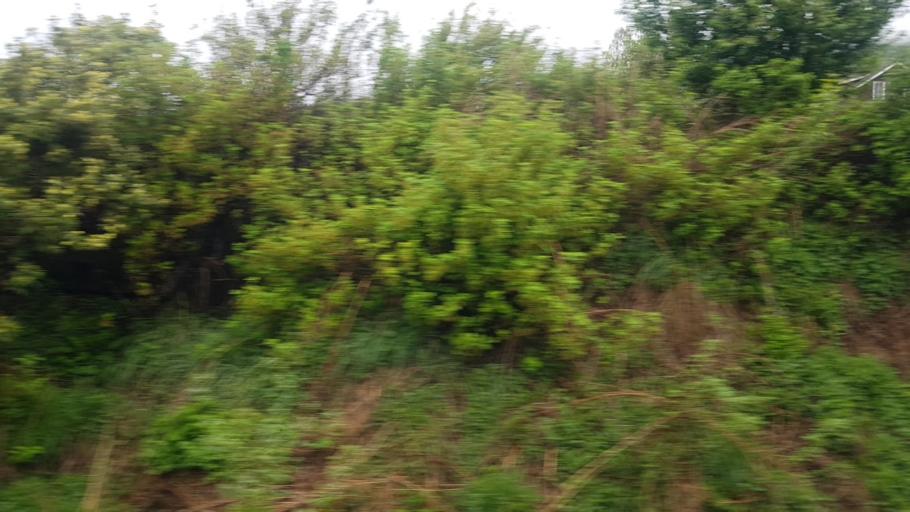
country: NO
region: Oppland
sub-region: Sor-Fron
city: Hundorp
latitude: 61.5561
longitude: 9.9421
